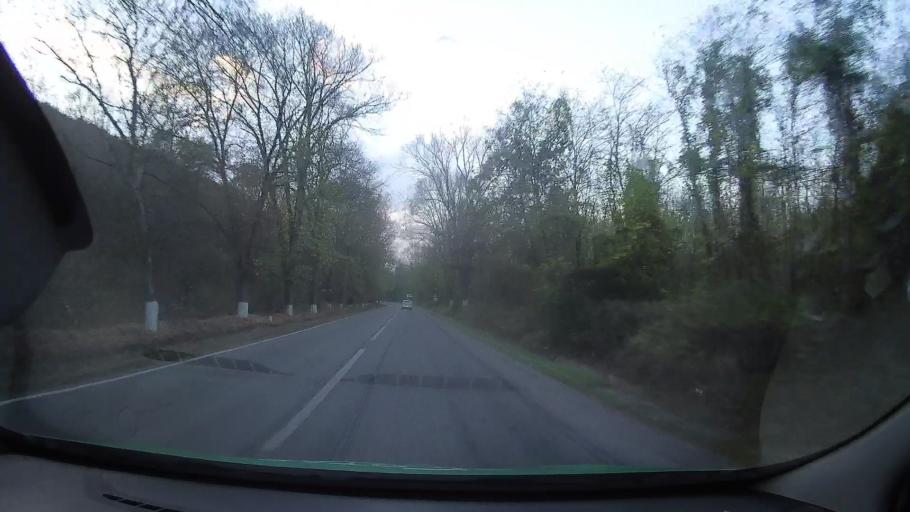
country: RO
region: Constanta
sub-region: Comuna Lipnita
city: Lipnita
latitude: 44.0951
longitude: 27.6521
